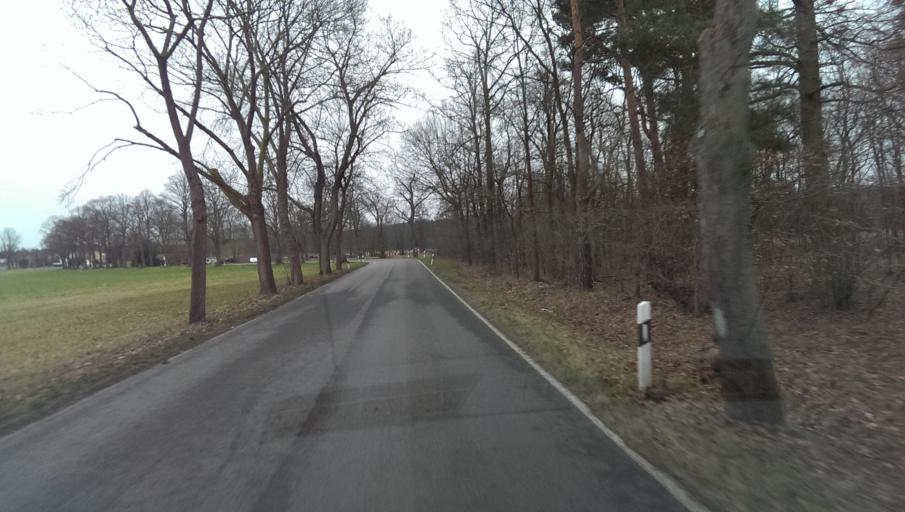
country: DE
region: Brandenburg
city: Mittenwalde
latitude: 52.2167
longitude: 13.5499
